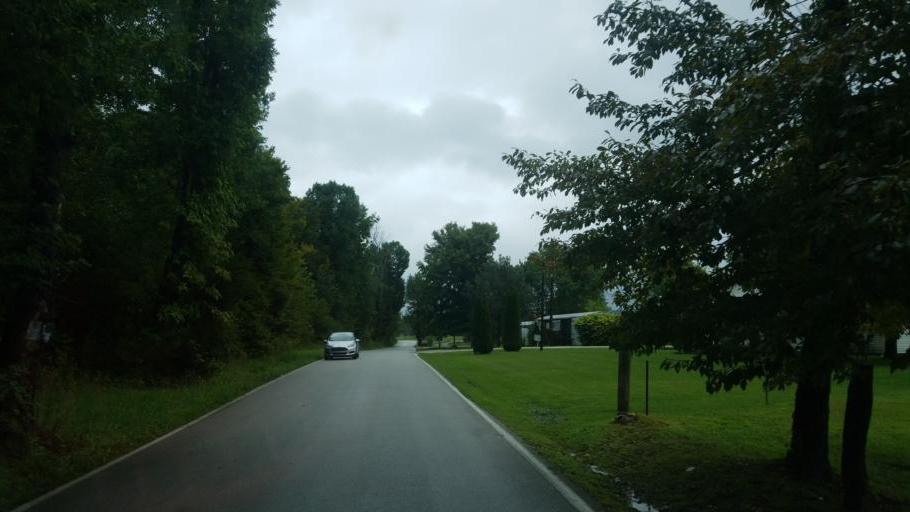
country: US
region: Kentucky
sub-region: Rowan County
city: Morehead
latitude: 38.1555
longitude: -83.5083
